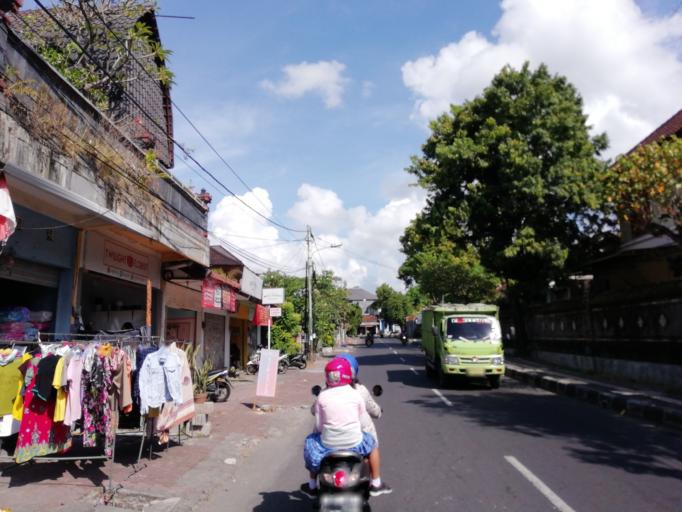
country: ID
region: Bali
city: Denpasar
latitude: -8.6736
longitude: 115.2173
